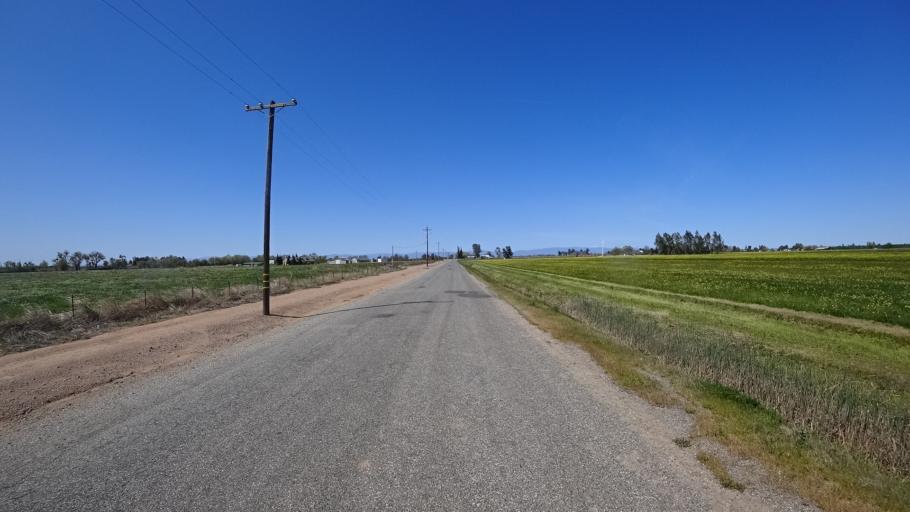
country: US
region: California
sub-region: Glenn County
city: Hamilton City
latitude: 39.7897
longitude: -122.0578
